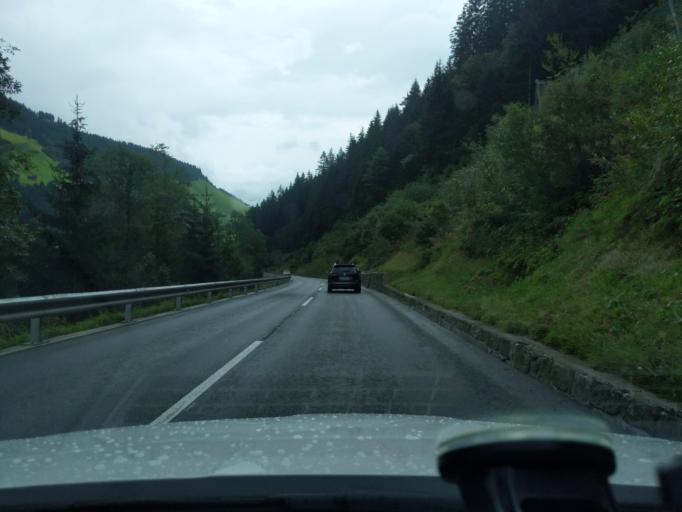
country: AT
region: Tyrol
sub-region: Politischer Bezirk Schwaz
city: Schwendau
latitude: 47.1599
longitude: 11.7534
